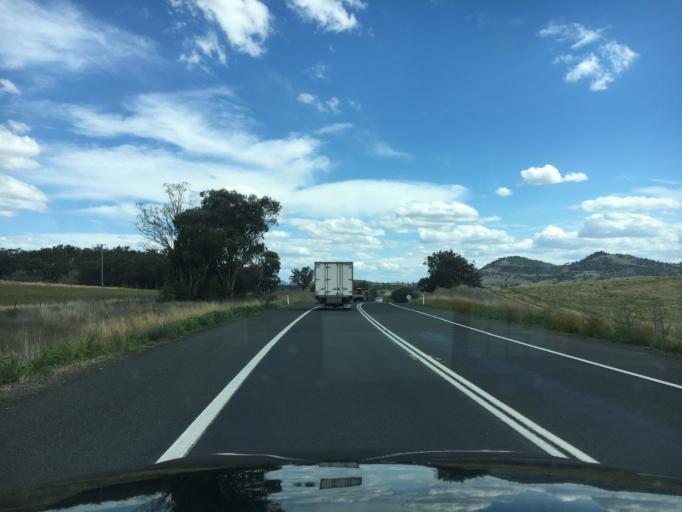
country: AU
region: New South Wales
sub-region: Liverpool Plains
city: Quirindi
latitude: -31.4650
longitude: 150.8612
